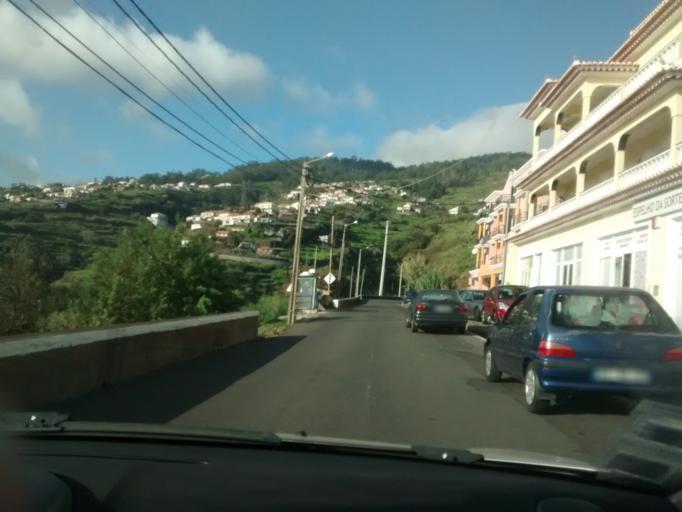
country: PT
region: Madeira
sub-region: Calheta
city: Estreito da Calheta
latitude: 32.7310
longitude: -17.1781
